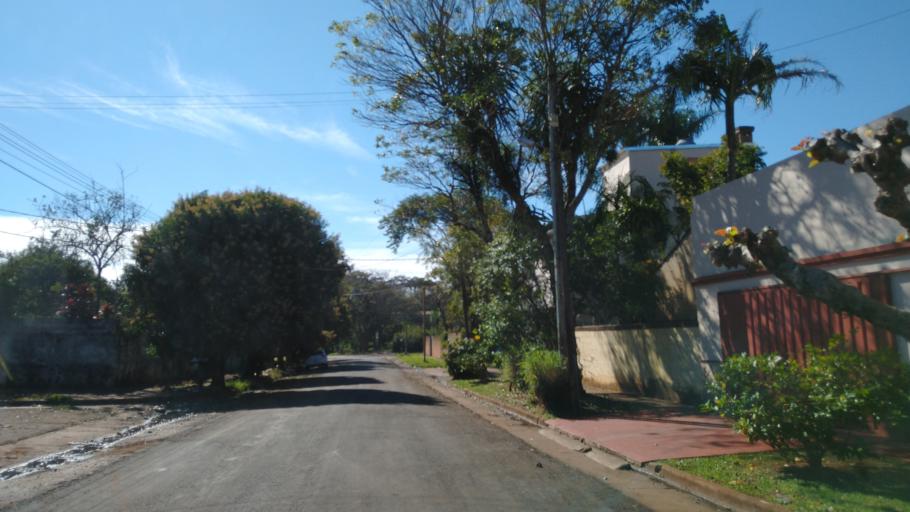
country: AR
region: Misiones
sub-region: Departamento de Capital
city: Posadas
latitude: -27.3643
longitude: -55.9370
